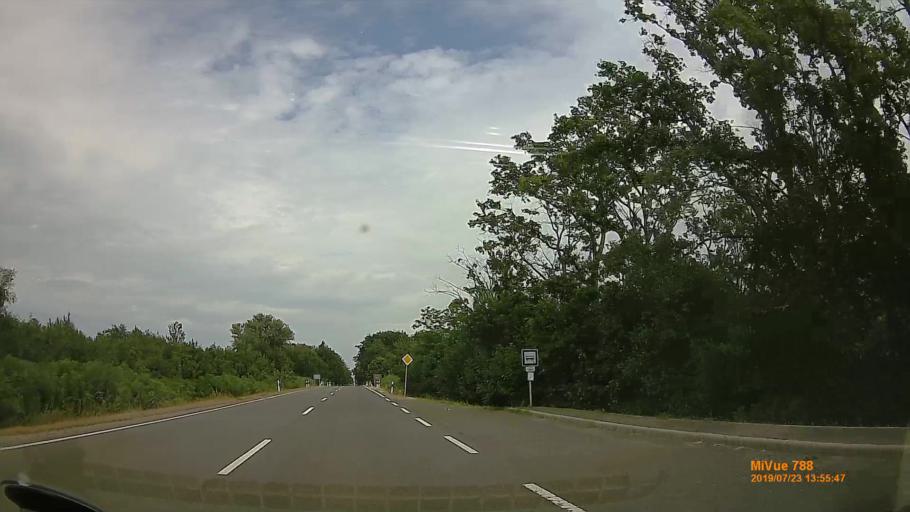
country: HU
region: Hajdu-Bihar
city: Gorbehaza
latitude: 47.9226
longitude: 21.2226
